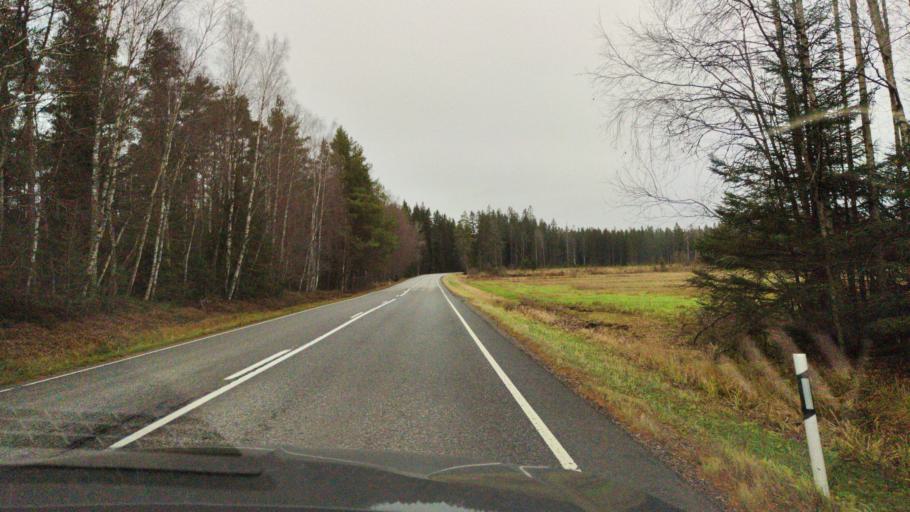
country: FI
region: Varsinais-Suomi
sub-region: Loimaa
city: Ylaene
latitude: 60.7513
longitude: 22.4272
